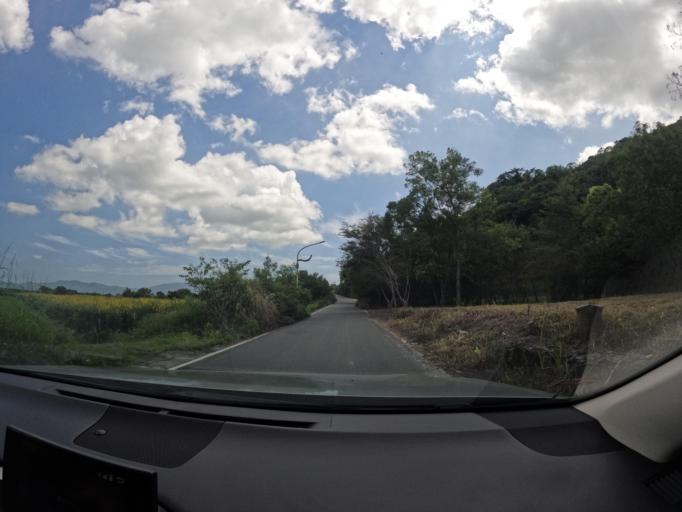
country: TW
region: Taiwan
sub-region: Hualien
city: Hualian
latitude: 23.7181
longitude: 121.4071
